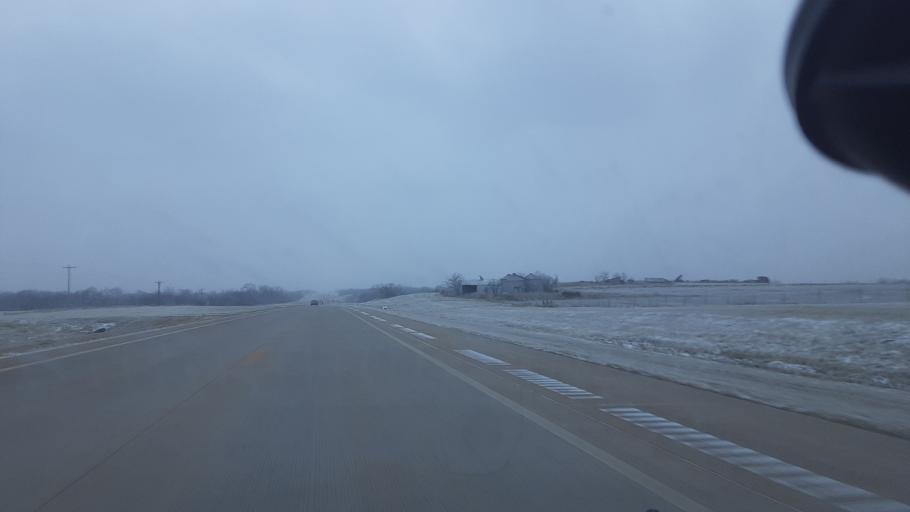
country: US
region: Oklahoma
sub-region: Payne County
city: Perkins
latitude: 35.9860
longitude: -97.1082
